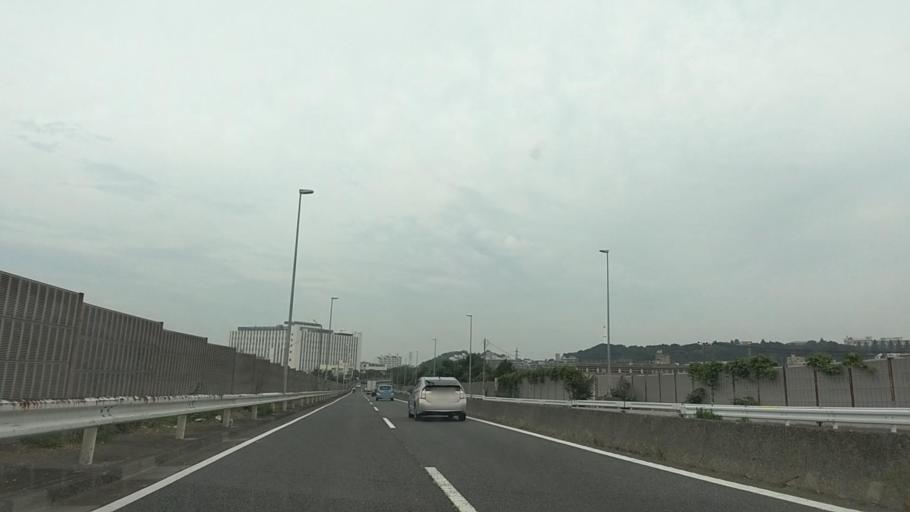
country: JP
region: Kanagawa
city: Fujisawa
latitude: 35.3546
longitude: 139.4865
